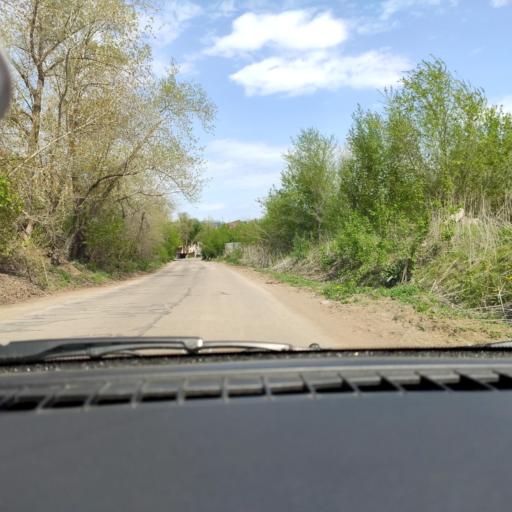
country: RU
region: Samara
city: Samara
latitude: 53.1790
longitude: 50.1248
